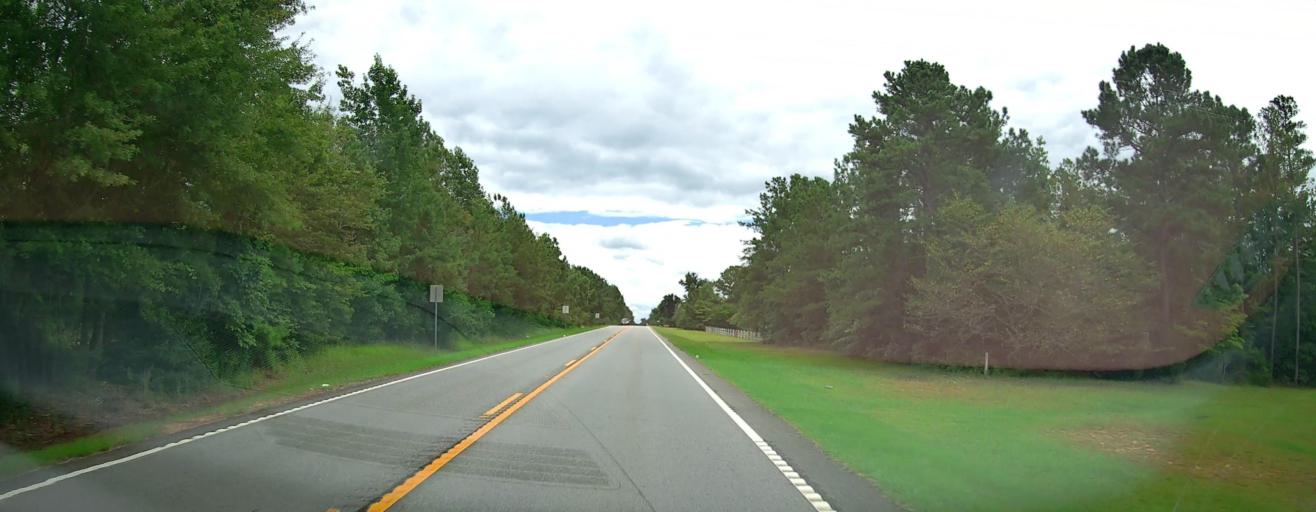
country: US
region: Georgia
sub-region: Twiggs County
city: Jeffersonville
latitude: 32.6724
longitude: -83.3298
